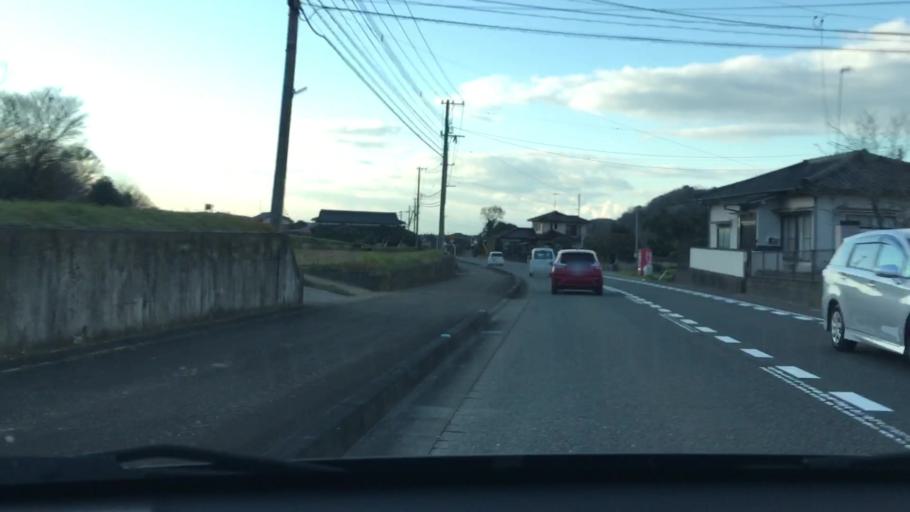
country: JP
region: Oita
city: Bungo-Takada-shi
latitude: 33.5011
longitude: 131.3740
